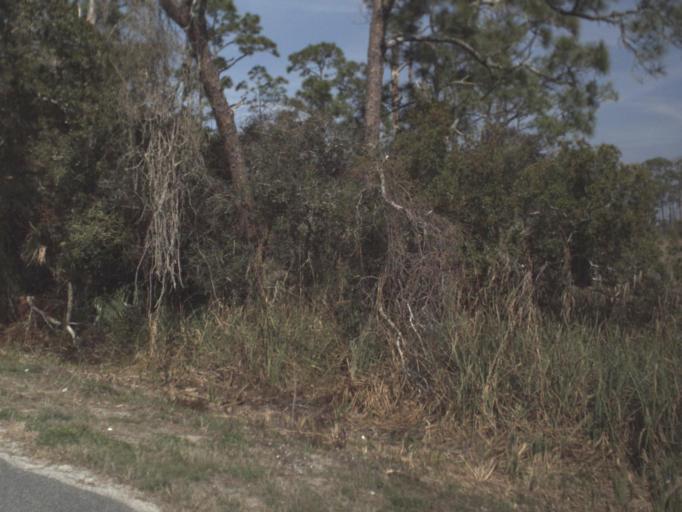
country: US
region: Florida
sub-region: Franklin County
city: Carrabelle
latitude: 29.8366
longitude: -84.6824
